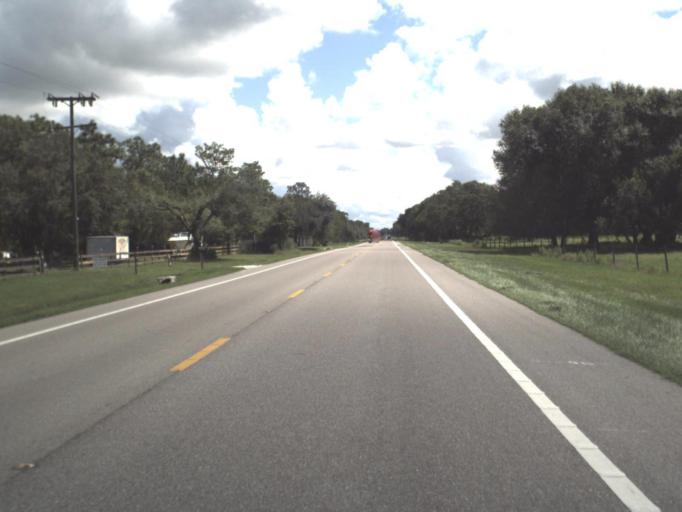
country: US
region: Florida
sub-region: Sarasota County
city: Lake Sarasota
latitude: 27.3591
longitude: -82.1899
